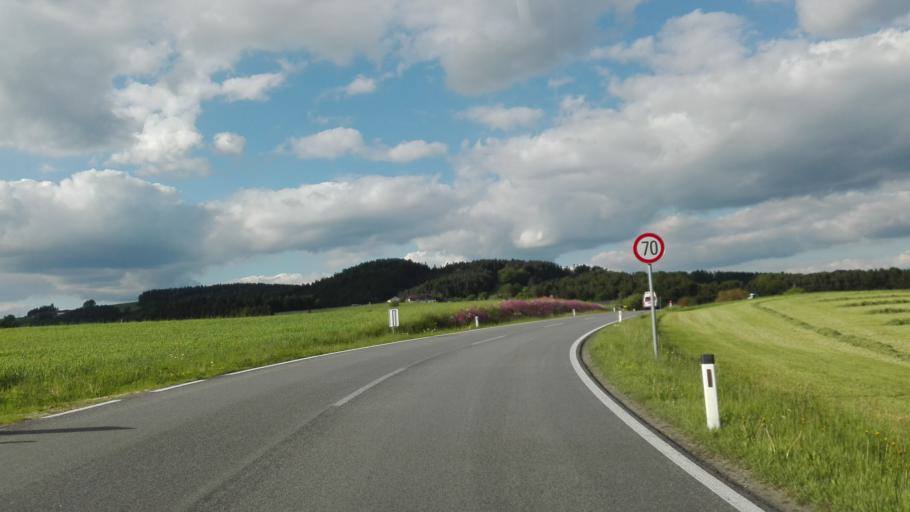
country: AT
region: Upper Austria
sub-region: Politischer Bezirk Perg
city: Perg
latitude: 48.3796
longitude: 14.7029
